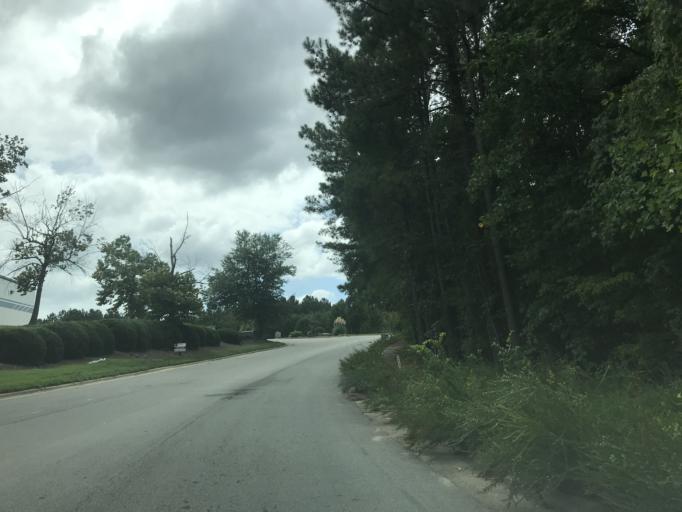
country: US
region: North Carolina
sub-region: Wake County
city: Raleigh
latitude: 35.7925
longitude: -78.5688
